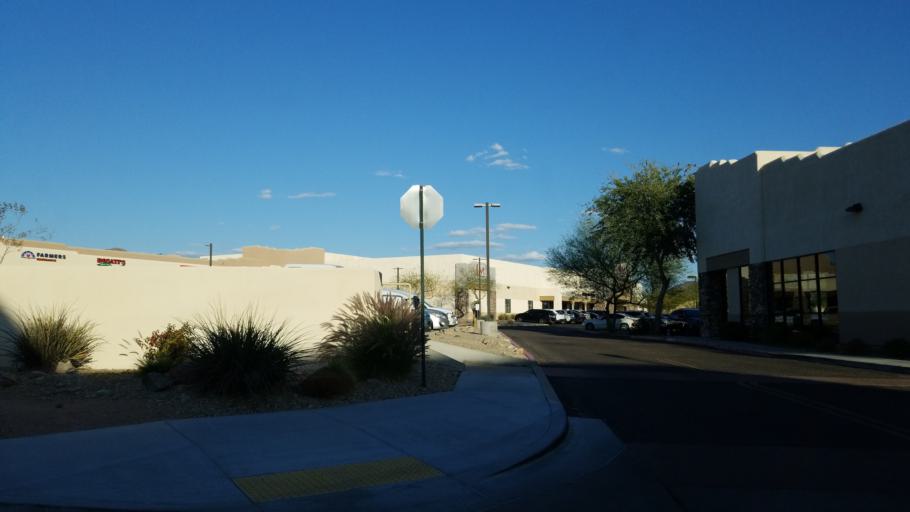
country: US
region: Arizona
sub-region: Maricopa County
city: Scottsdale
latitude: 33.5844
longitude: -111.8308
